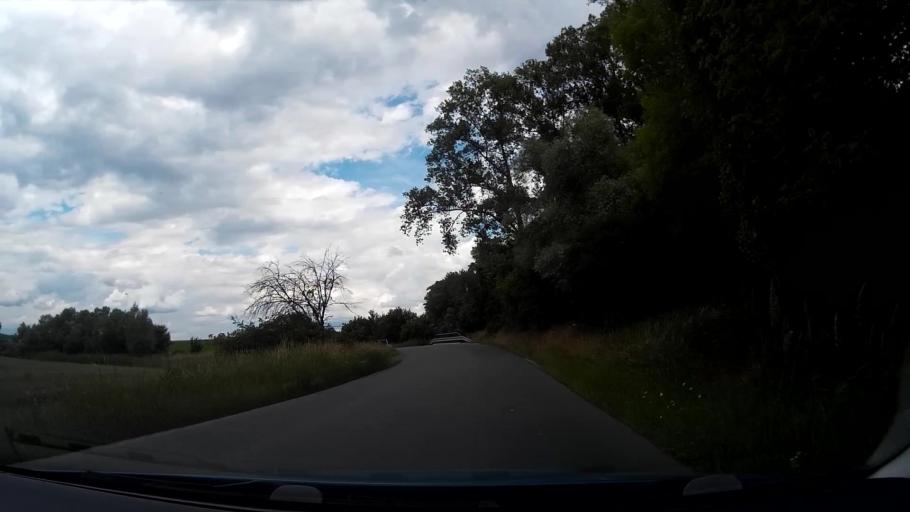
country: CZ
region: South Moravian
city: Ostopovice
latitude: 49.1484
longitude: 16.5277
